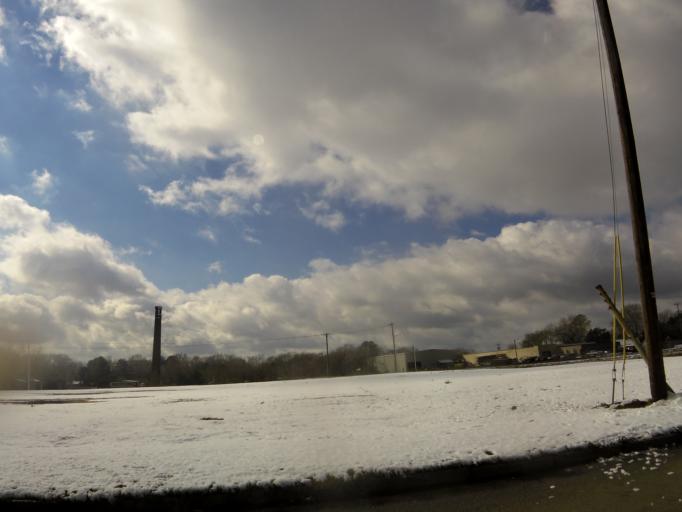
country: US
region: North Carolina
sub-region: Wilson County
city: Wilson
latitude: 35.7208
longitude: -77.9080
